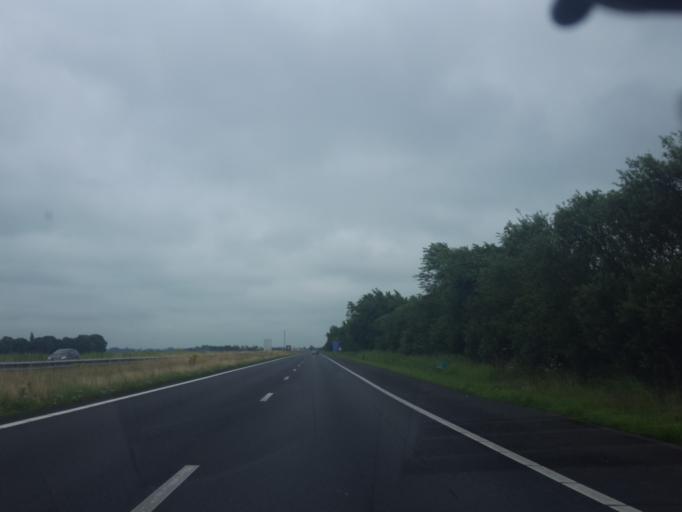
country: NL
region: Friesland
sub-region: Gemeente Leeuwarden
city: Wirdum
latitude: 53.1399
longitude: 5.7982
